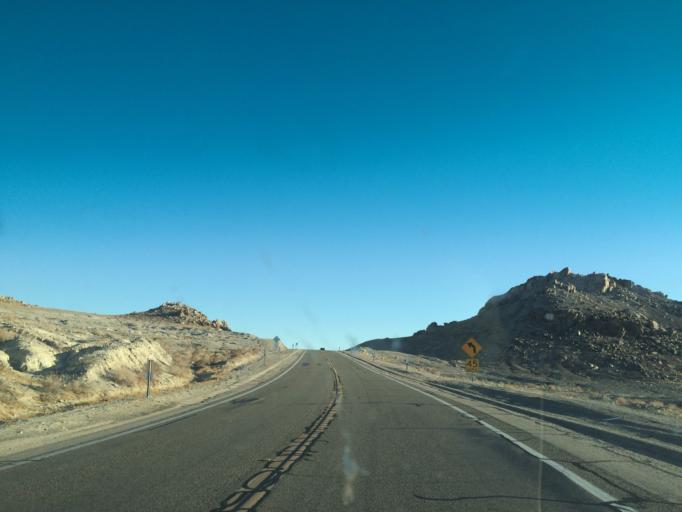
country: US
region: California
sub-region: San Bernardino County
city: Searles Valley
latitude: 35.6851
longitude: -117.3842
